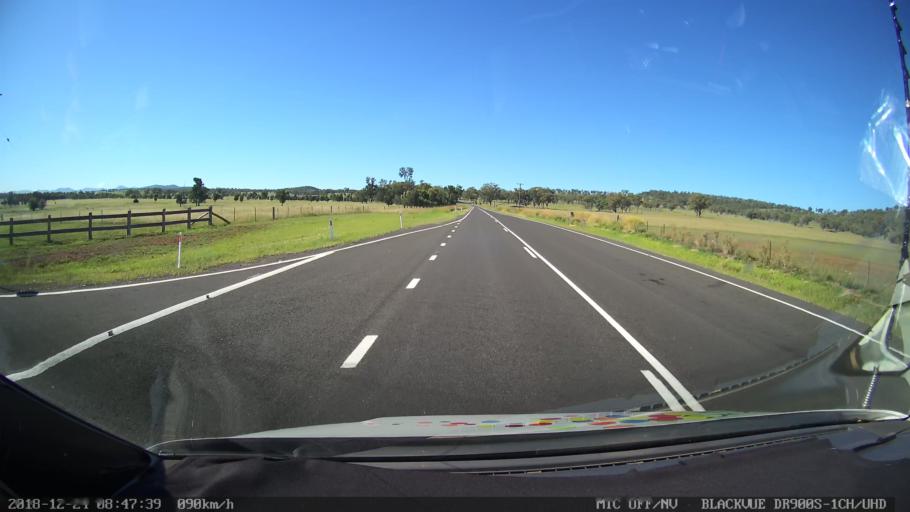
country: AU
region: New South Wales
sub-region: Liverpool Plains
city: Quirindi
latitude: -31.4450
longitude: 150.6471
